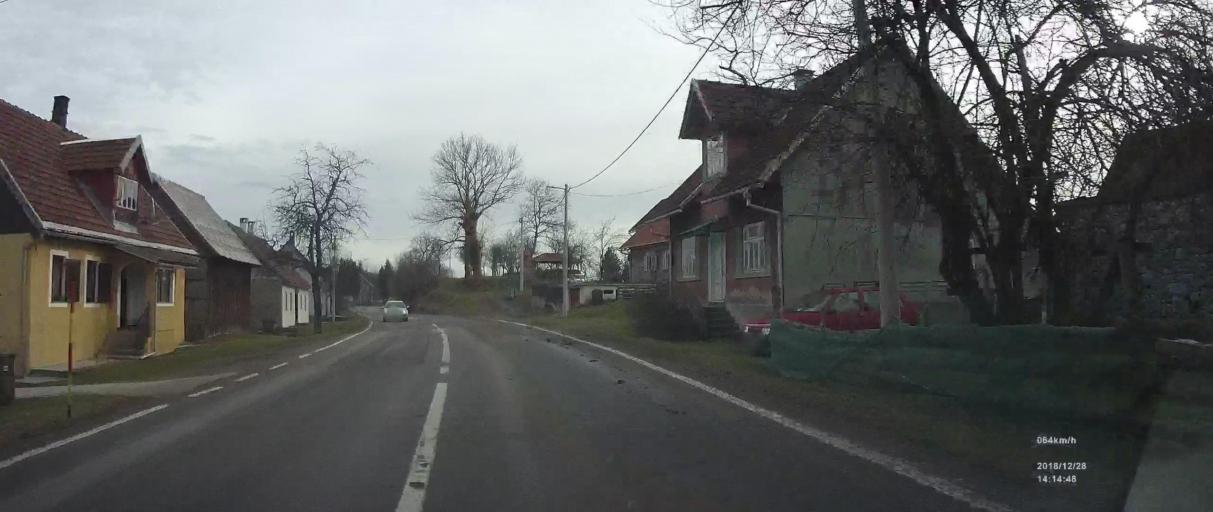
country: HR
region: Primorsko-Goranska
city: Vrbovsko
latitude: 45.4292
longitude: 15.0223
